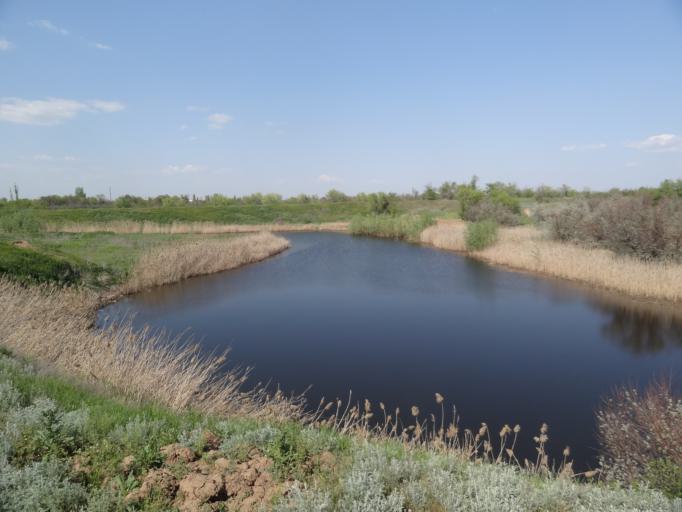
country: RU
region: Saratov
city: Privolzhskiy
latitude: 51.3976
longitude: 46.0718
